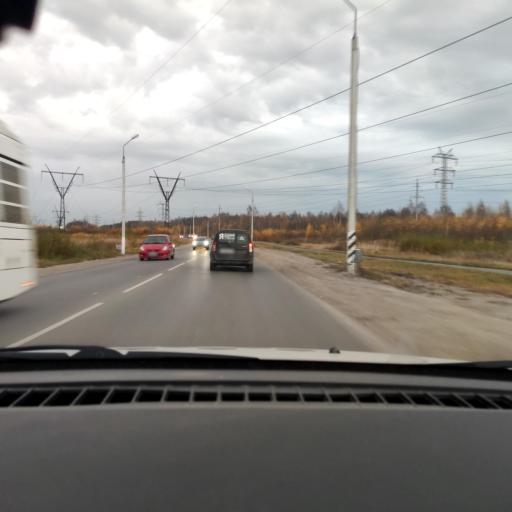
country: RU
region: Perm
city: Perm
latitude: 58.1006
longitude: 56.3909
